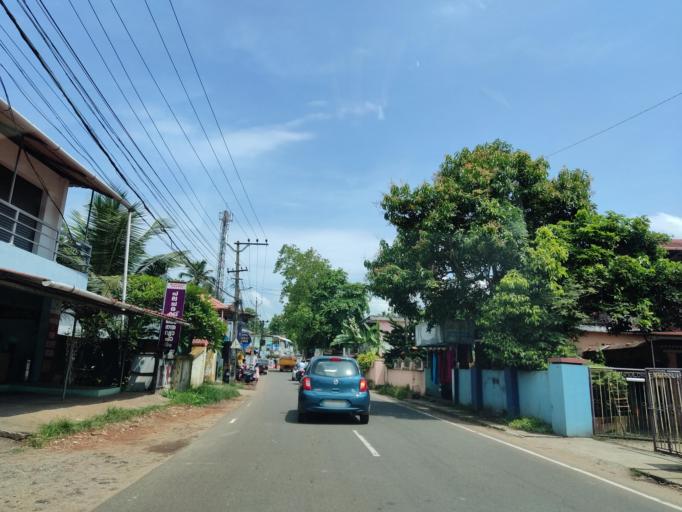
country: IN
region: Kerala
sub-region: Alappuzha
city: Chengannur
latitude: 9.3028
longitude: 76.5870
